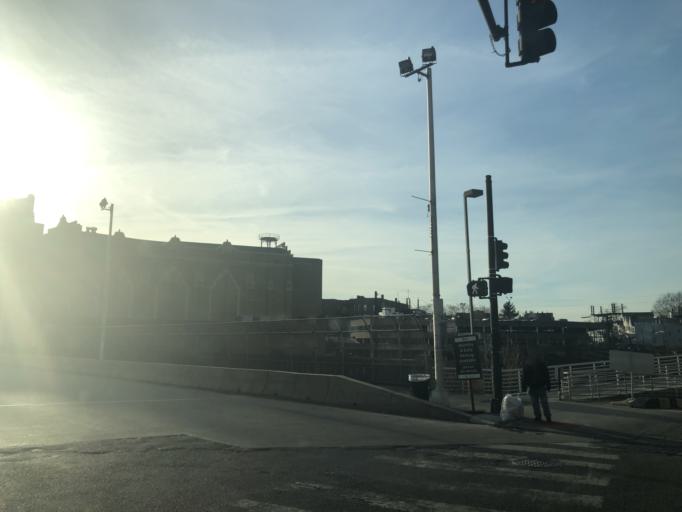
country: US
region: New Jersey
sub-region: Hudson County
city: Jersey City
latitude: 40.7331
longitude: -74.0630
